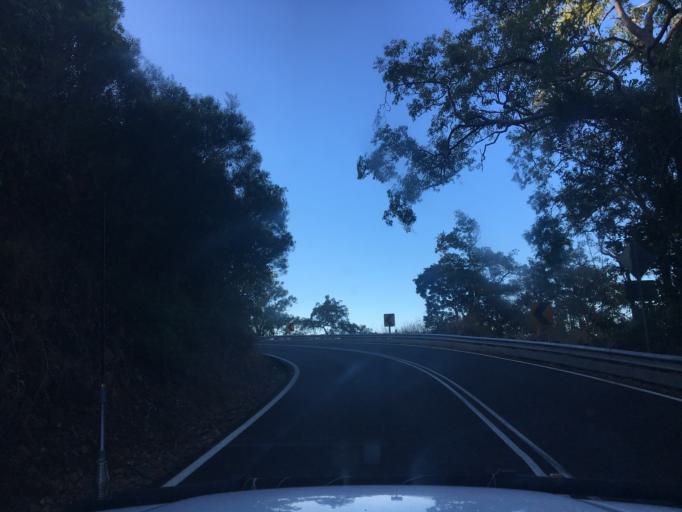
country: AU
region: Queensland
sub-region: Cairns
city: Port Douglas
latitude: -16.6282
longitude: 145.5483
